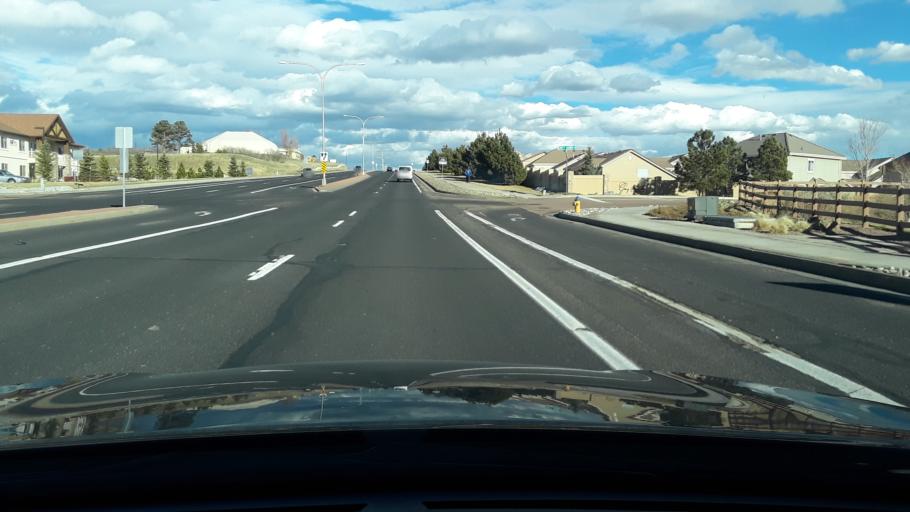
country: US
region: Colorado
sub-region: El Paso County
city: Gleneagle
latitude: 39.0272
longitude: -104.8143
